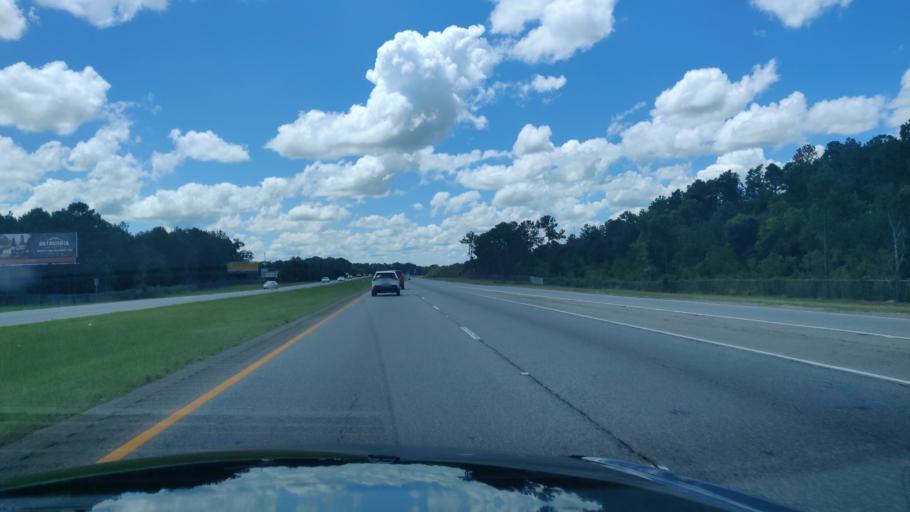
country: US
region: Georgia
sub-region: Dougherty County
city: Albany
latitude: 31.5928
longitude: -84.1279
